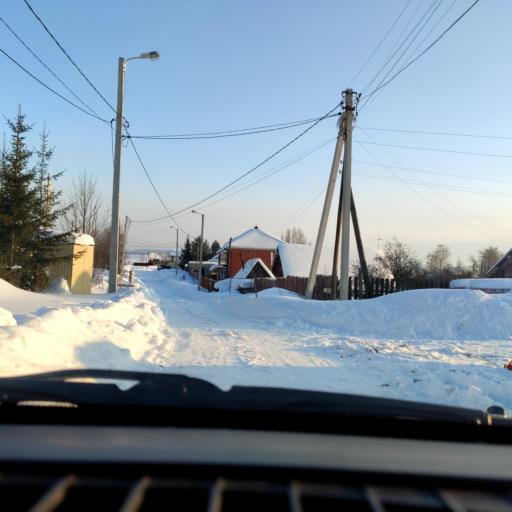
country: RU
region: Perm
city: Froly
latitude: 57.9502
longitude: 56.3051
